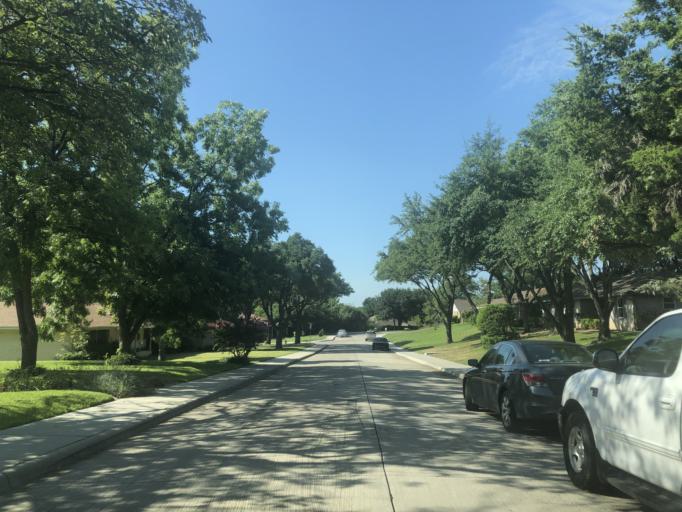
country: US
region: Texas
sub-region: Dallas County
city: Grand Prairie
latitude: 32.7568
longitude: -97.0173
